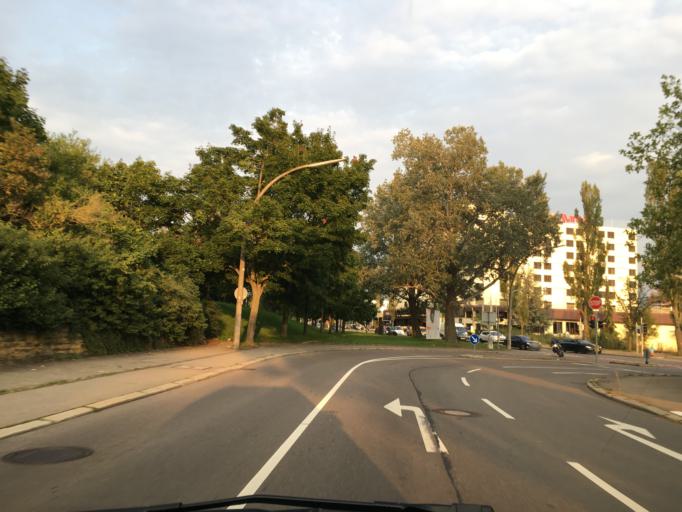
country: DE
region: Baden-Wuerttemberg
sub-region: Regierungsbezirk Stuttgart
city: Sindelfingen
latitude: 48.7074
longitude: 9.0197
